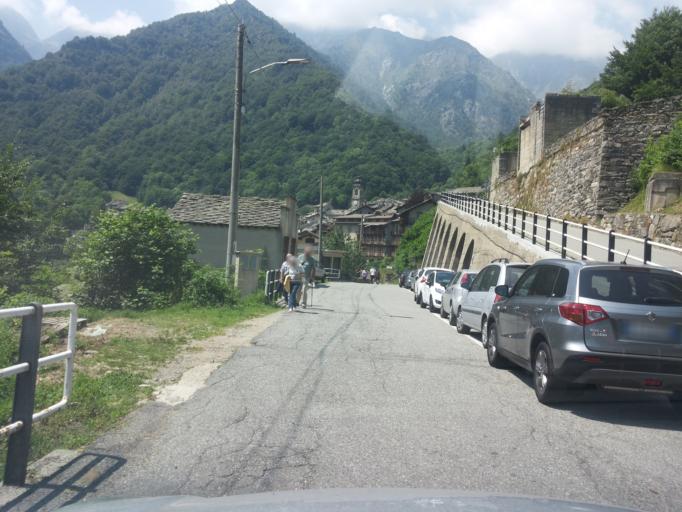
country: IT
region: Piedmont
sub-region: Provincia di Biella
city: Piedicavallo
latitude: 45.6876
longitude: 7.9588
